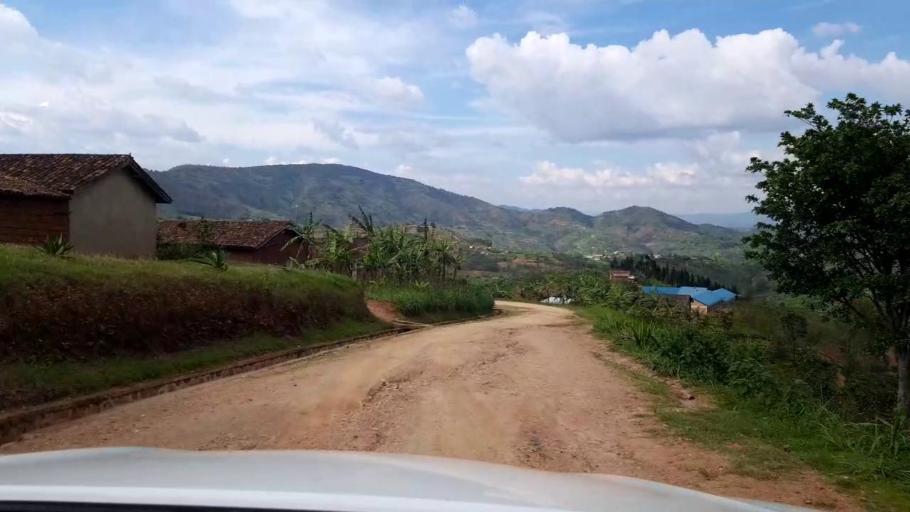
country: RW
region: Southern Province
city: Gitarama
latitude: -1.9795
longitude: 29.7108
